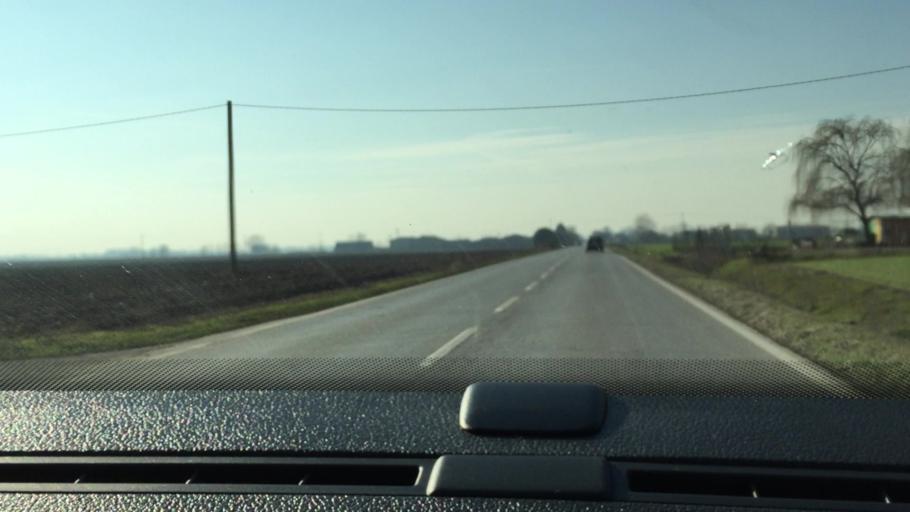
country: IT
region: Lombardy
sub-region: Provincia di Mantova
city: Rodigo
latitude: 45.2291
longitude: 10.6295
